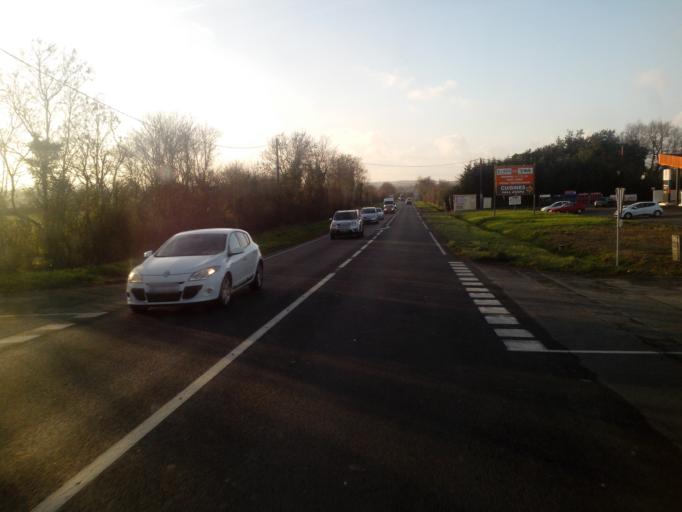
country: FR
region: Pays de la Loire
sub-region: Departement de Maine-et-Loire
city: La Seguiniere
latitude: 47.0592
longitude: -0.9116
